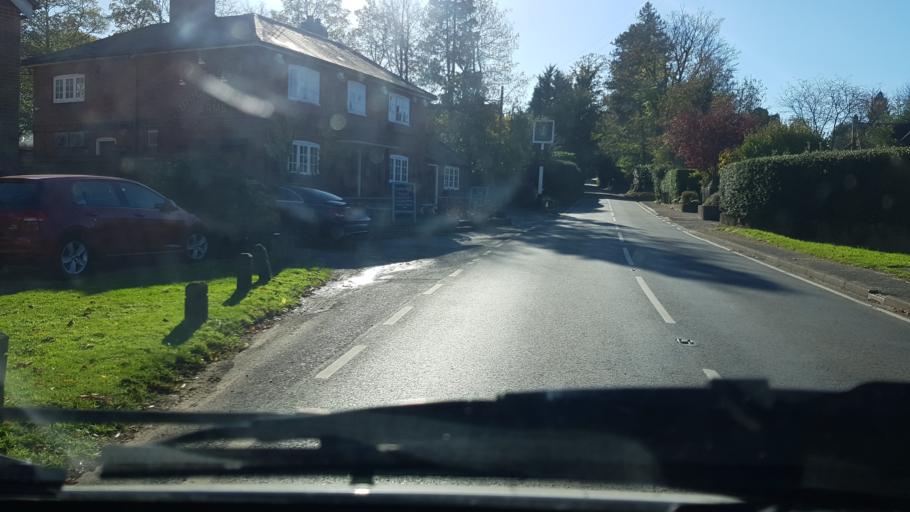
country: GB
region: England
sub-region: Surrey
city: Chilworth
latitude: 51.1831
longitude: -0.5237
